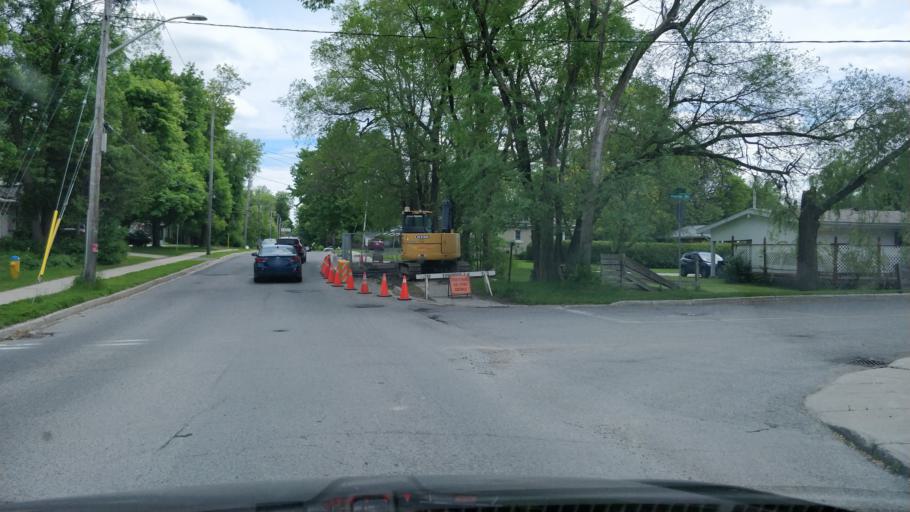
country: CA
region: Ontario
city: Perth
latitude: 44.9074
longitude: -76.2560
